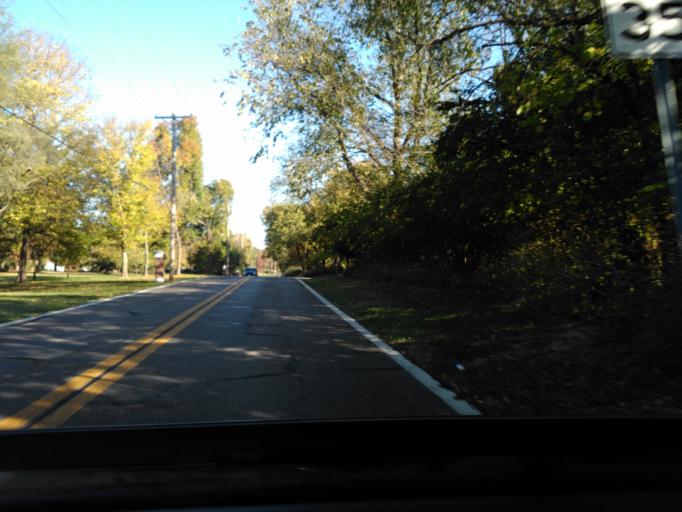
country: US
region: Missouri
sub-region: Saint Louis County
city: Town and Country
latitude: 38.6072
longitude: -90.4854
